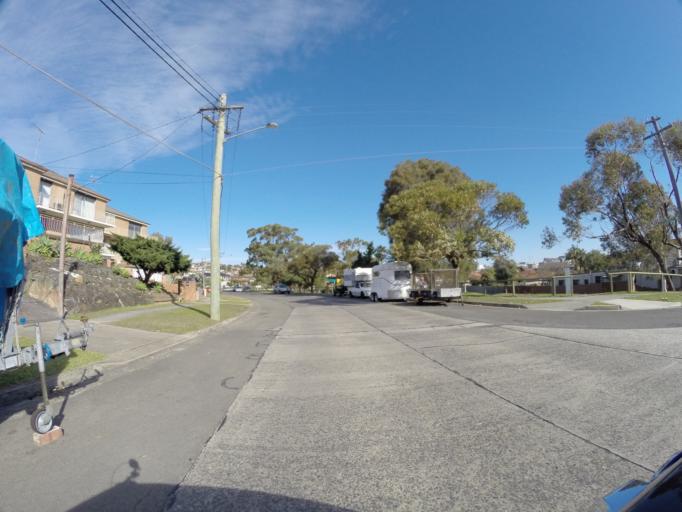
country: AU
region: New South Wales
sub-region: Randwick
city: Daceyville
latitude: -33.9367
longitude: 151.2450
